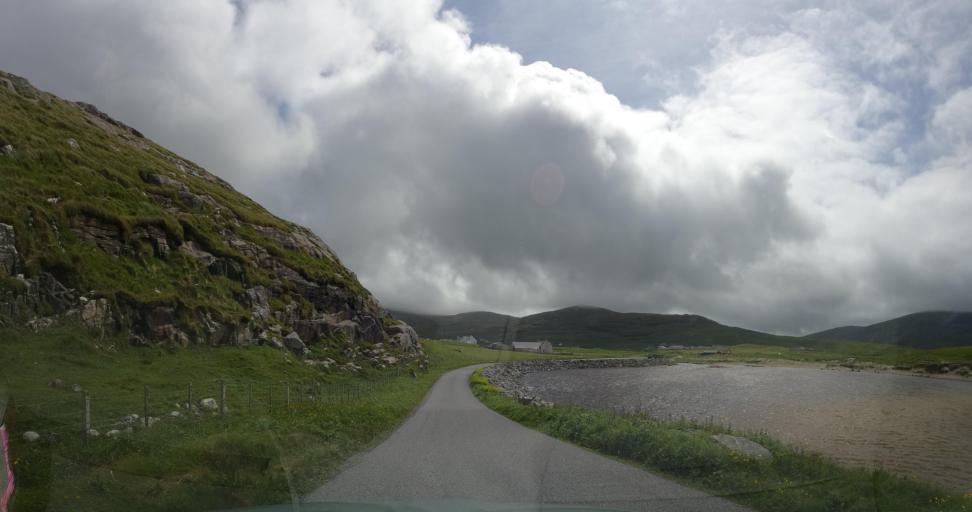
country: GB
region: Scotland
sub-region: Eilean Siar
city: Barra
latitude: 56.9888
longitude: -7.5089
